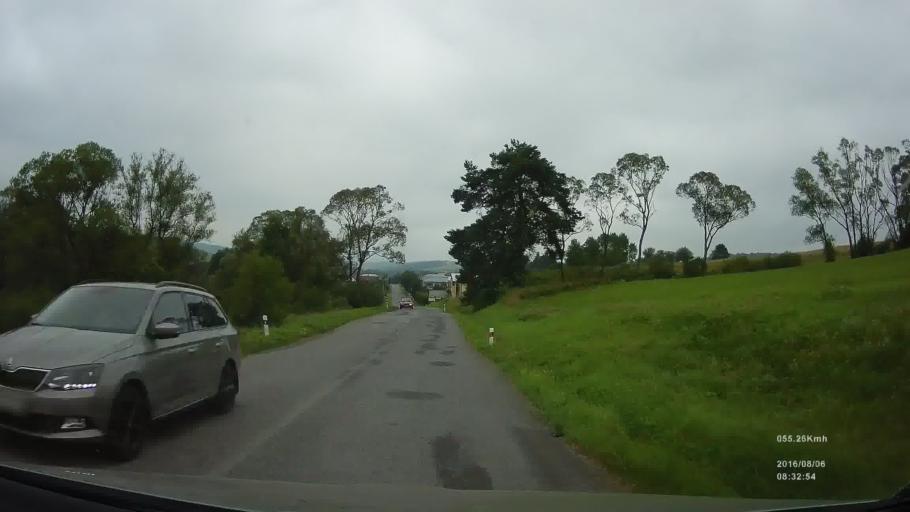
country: SK
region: Presovsky
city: Svidnik
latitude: 49.3398
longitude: 21.5974
